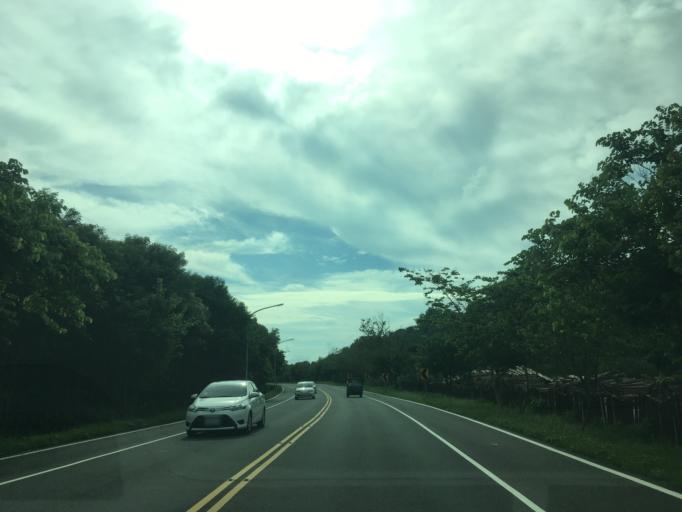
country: TW
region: Taiwan
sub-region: Chiayi
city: Jiayi Shi
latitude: 23.4520
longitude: 120.5656
